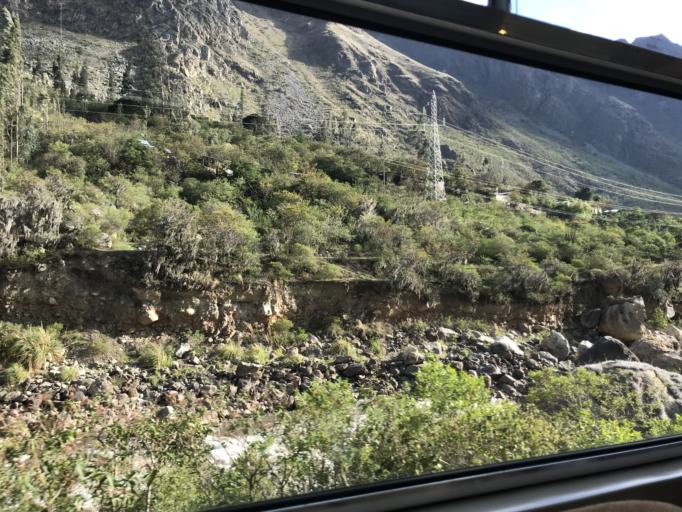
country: PE
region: Cusco
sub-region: Provincia de Urubamba
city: Ollantaytambo
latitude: -13.2266
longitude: -72.4011
